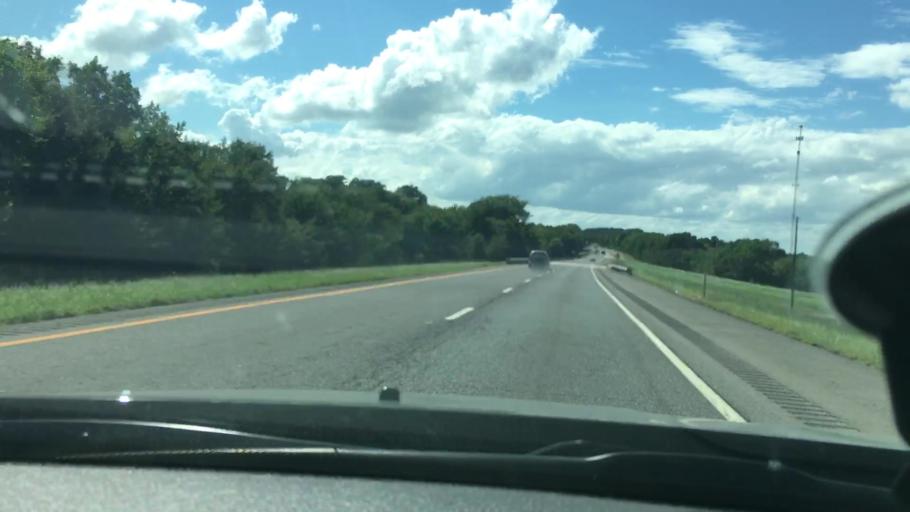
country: US
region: Oklahoma
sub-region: Sequoyah County
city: Vian
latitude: 35.4901
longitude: -95.0774
